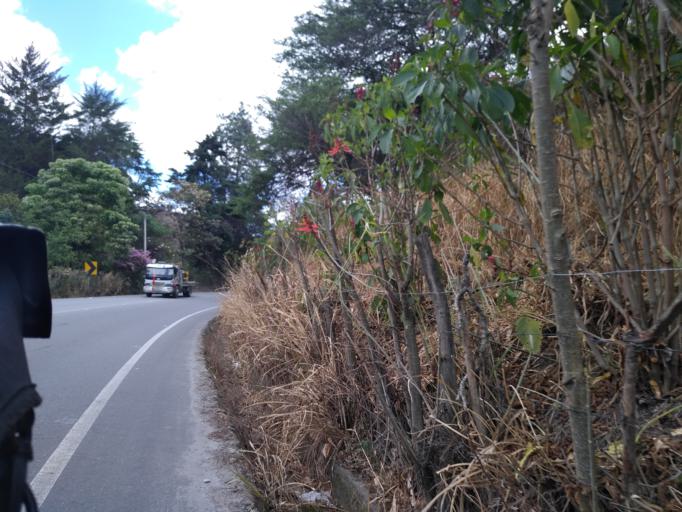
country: EC
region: Loja
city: Loja
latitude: -4.2120
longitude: -79.2306
